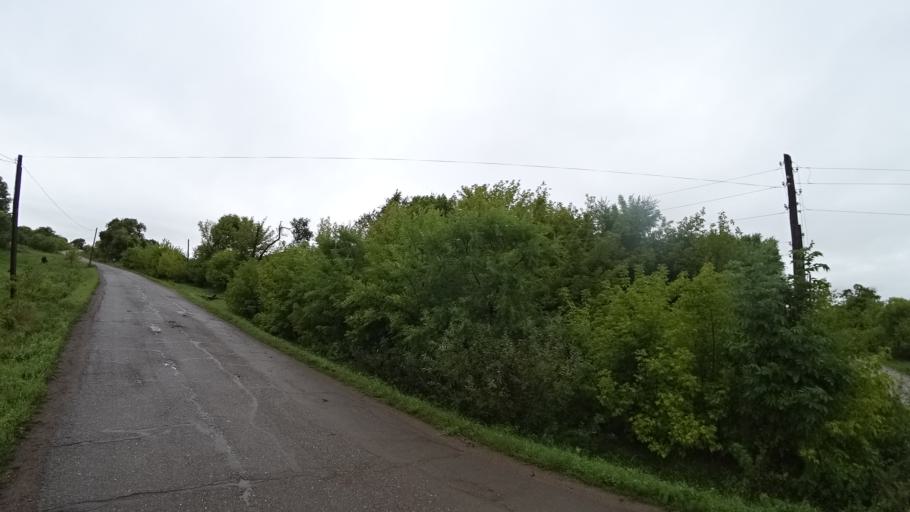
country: RU
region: Primorskiy
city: Monastyrishche
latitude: 44.2564
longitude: 132.4247
